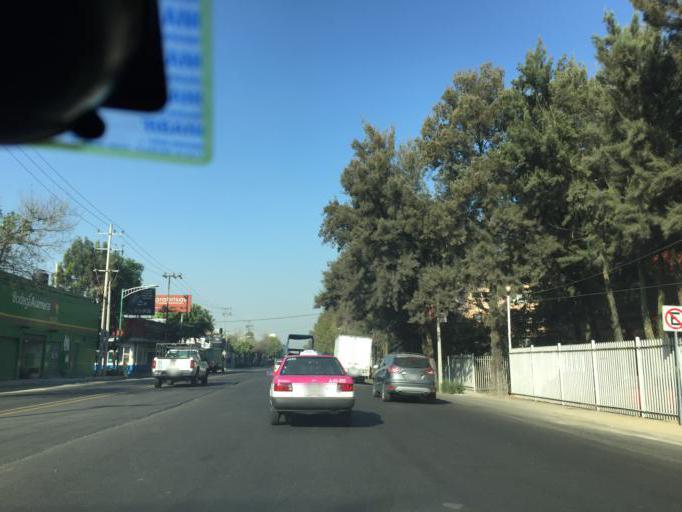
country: MX
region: Mexico
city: Colonia Lindavista
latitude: 19.4942
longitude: -99.1496
